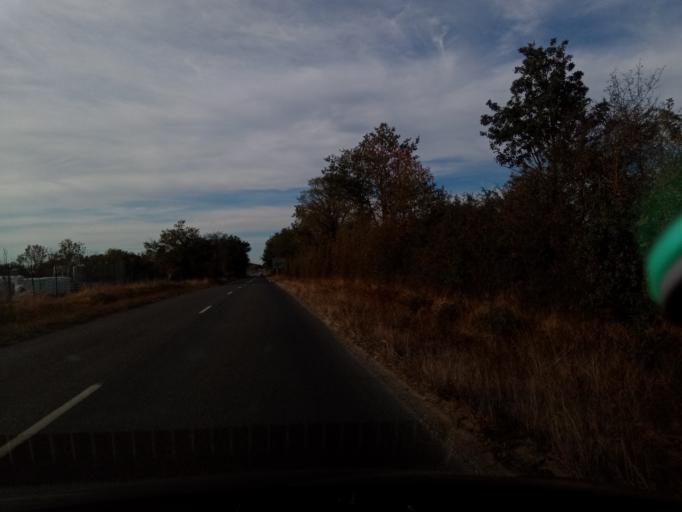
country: FR
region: Poitou-Charentes
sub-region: Departement de la Vienne
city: Saulge
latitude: 46.4027
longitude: 0.8941
